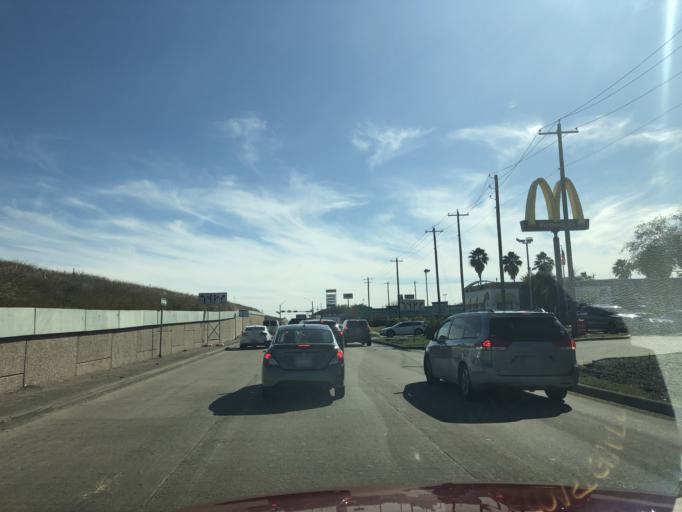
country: US
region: Texas
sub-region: Galveston County
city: League City
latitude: 29.5046
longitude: -95.1155
